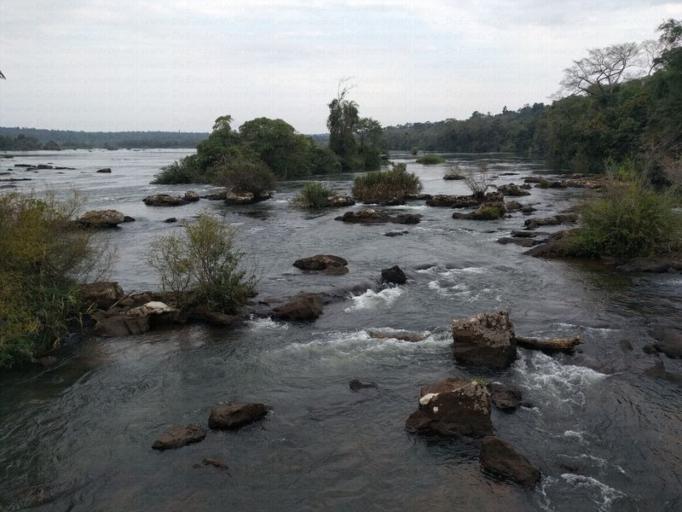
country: AR
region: Misiones
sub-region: Departamento de Iguazu
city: Puerto Iguazu
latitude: -25.6889
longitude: -54.4460
